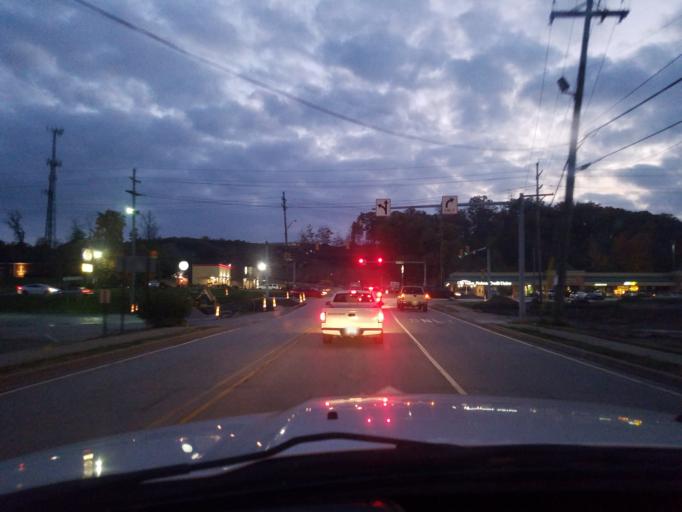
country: US
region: Indiana
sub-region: Floyd County
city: New Albany
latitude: 38.3094
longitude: -85.8432
